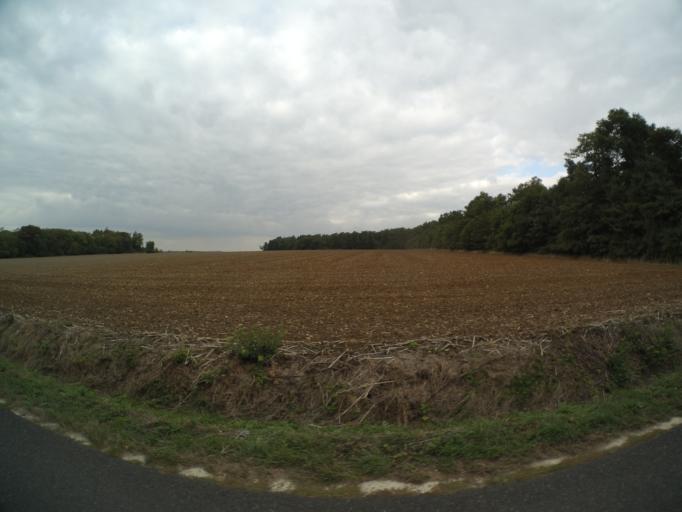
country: FR
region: Centre
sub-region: Departement d'Indre-et-Loire
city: Auzouer-en-Touraine
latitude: 47.5129
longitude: 0.9302
